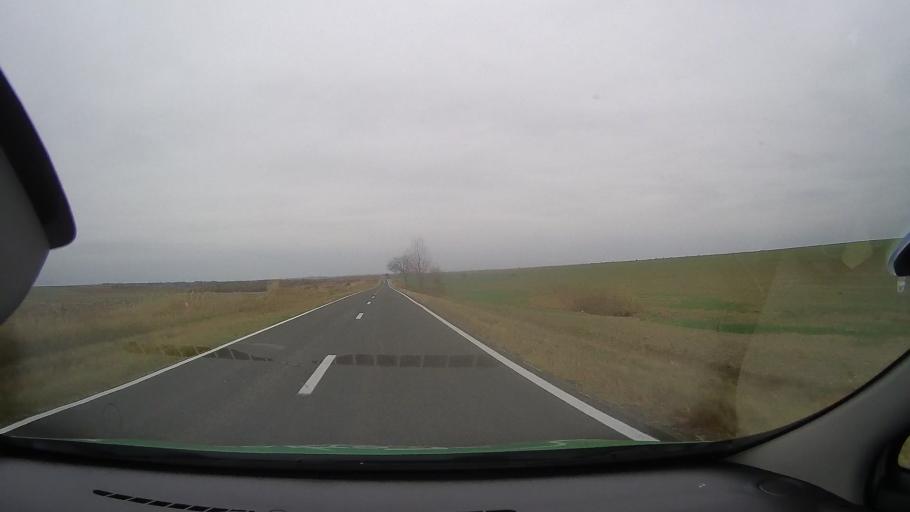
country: RO
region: Constanta
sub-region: Comuna Saraiu
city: Saraiu
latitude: 44.7109
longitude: 28.1017
